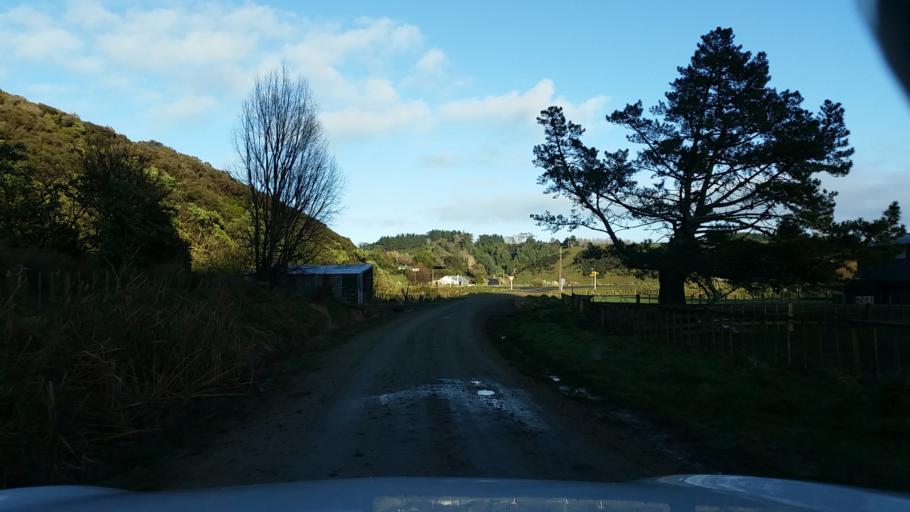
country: NZ
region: Taranaki
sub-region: South Taranaki District
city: Patea
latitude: -39.7597
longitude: 174.7304
